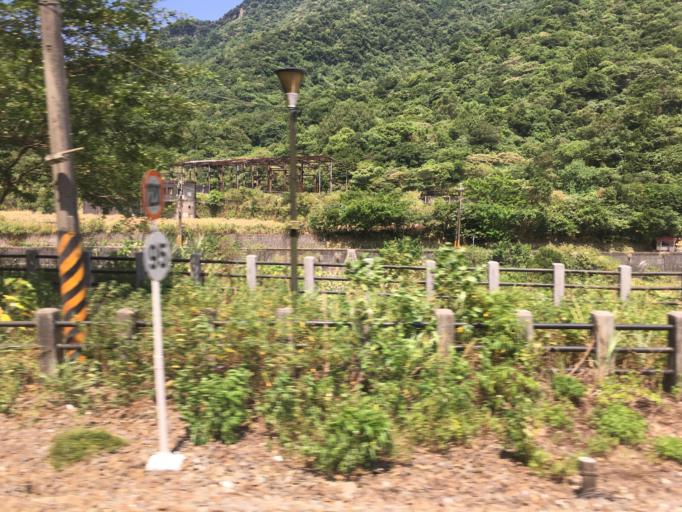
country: TW
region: Taiwan
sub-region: Keelung
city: Keelung
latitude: 25.1022
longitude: 121.8303
